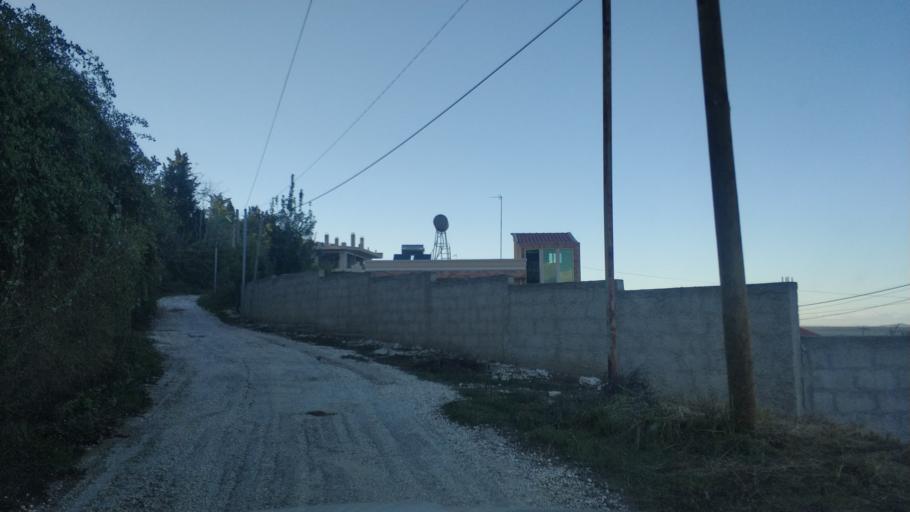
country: AL
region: Vlore
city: Vlore
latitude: 40.5137
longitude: 19.4193
